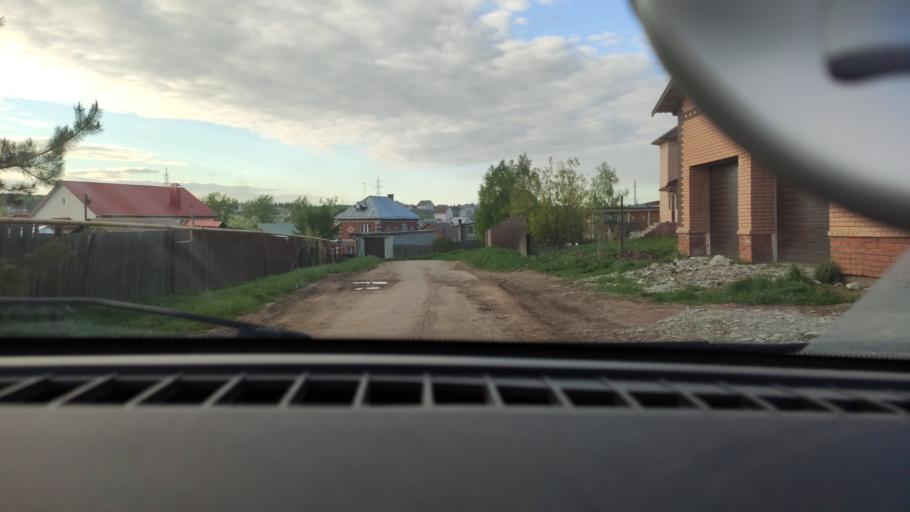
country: RU
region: Perm
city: Ferma
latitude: 57.9434
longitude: 56.3600
